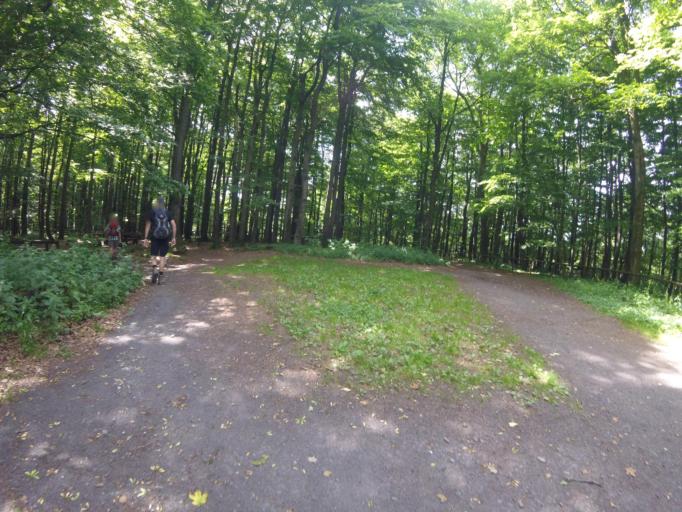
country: DE
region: Hesse
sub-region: Regierungsbezirk Giessen
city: Ulrichstein
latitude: 50.5171
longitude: 9.2383
